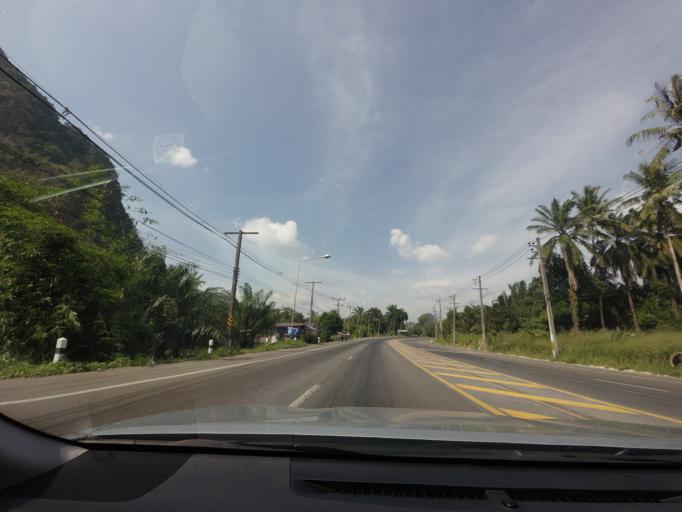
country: TH
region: Phangnga
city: Ban Ao Nang
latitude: 8.0821
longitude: 98.8039
